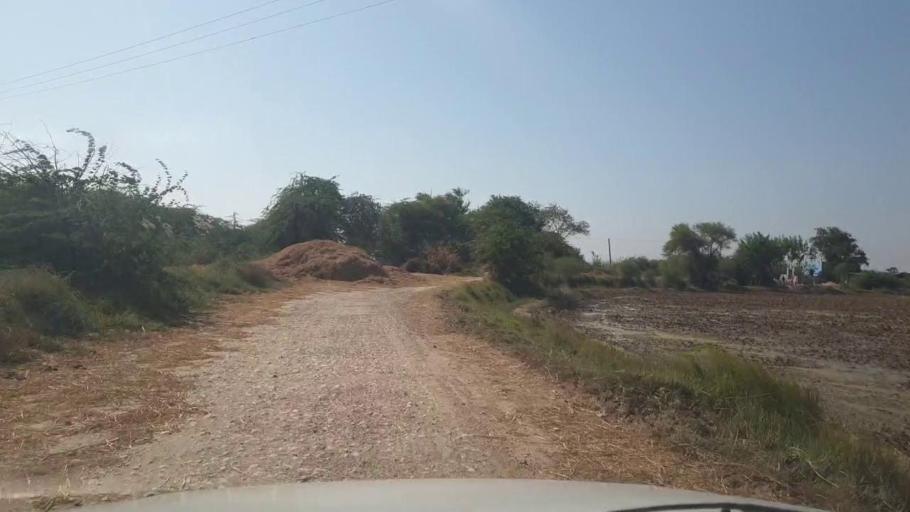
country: PK
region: Sindh
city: Chuhar Jamali
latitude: 24.4269
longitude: 67.7985
